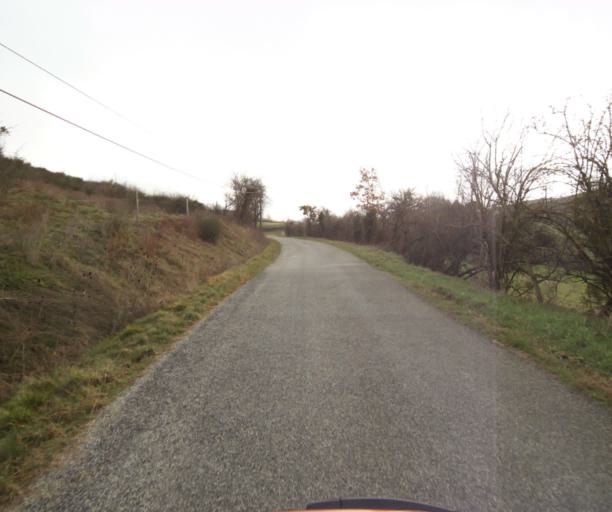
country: FR
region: Midi-Pyrenees
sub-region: Departement de la Haute-Garonne
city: Gaillac-Toulza
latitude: 43.1700
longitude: 1.5036
